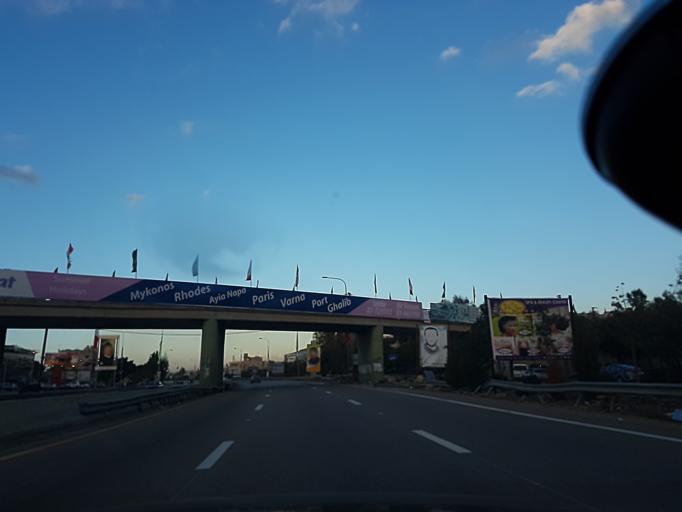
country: LB
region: Liban-Sud
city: Sidon
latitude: 33.5184
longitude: 35.3623
